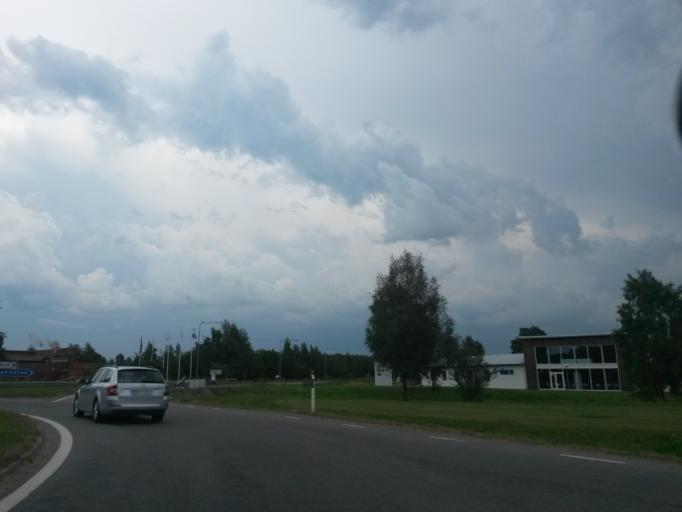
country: SE
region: Vaestra Goetaland
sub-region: Lidkopings Kommun
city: Lidkoping
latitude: 58.5027
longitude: 13.1254
